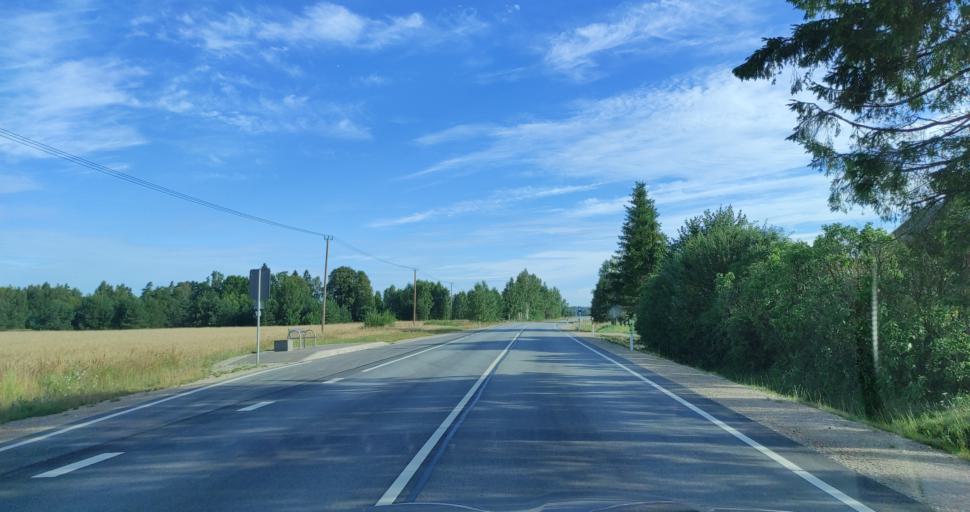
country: LV
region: Pavilostas
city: Pavilosta
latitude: 56.8134
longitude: 21.2262
